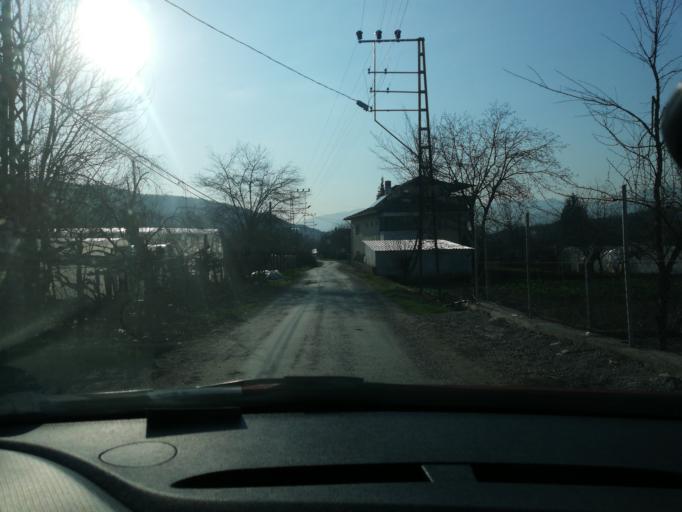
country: TR
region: Karabuk
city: Safranbolu
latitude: 41.2162
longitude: 32.7430
